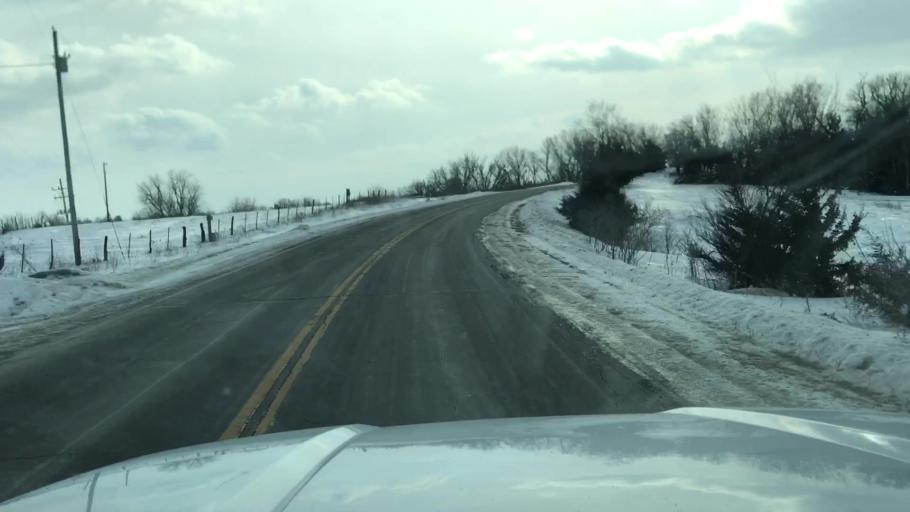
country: US
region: Missouri
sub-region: Gentry County
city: Stanberry
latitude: 40.3686
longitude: -94.6476
